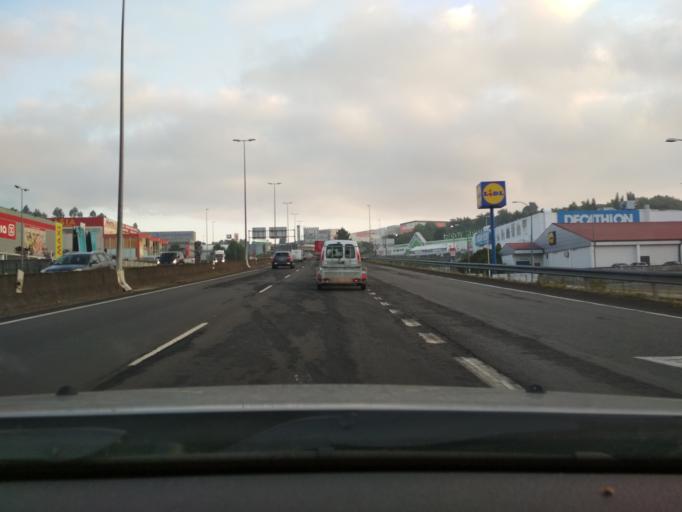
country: ES
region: Galicia
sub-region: Provincia da Coruna
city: Santiago de Compostela
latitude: 42.9002
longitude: -8.5105
